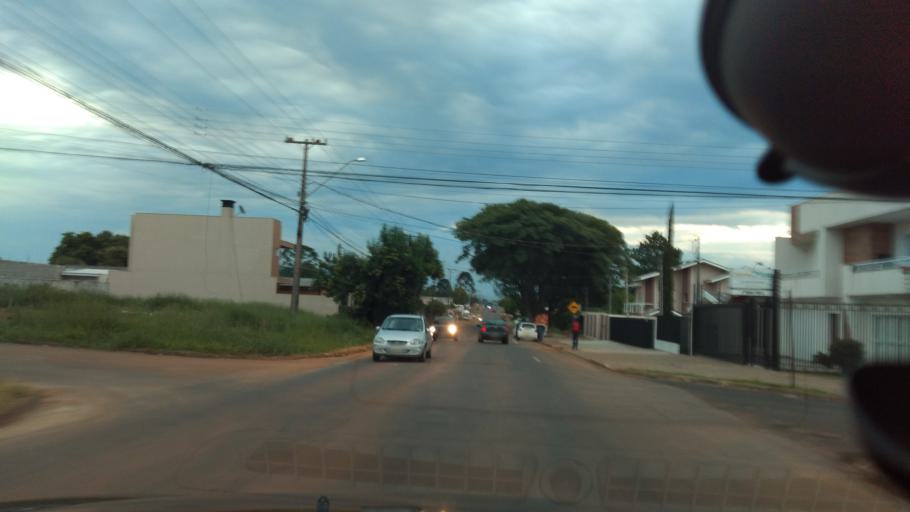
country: BR
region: Parana
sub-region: Guarapuava
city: Guarapuava
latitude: -25.3923
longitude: -51.4909
